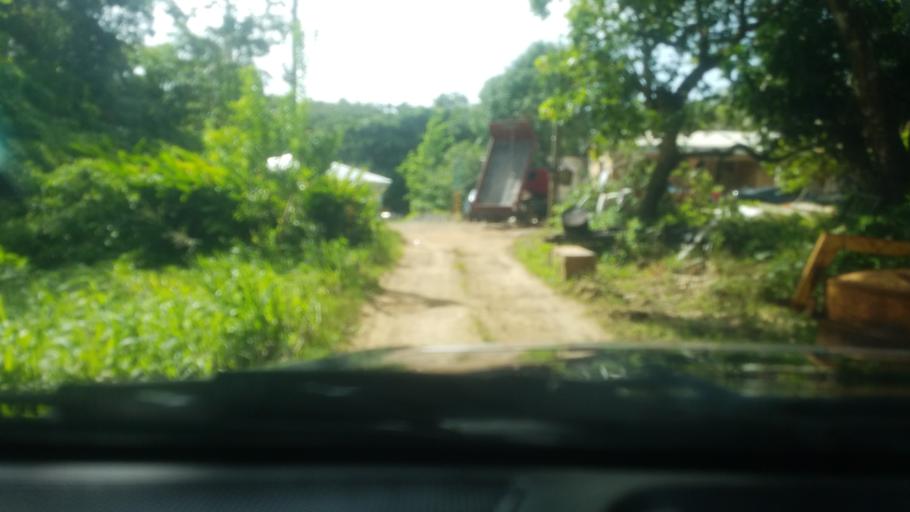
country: LC
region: Micoud Quarter
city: Micoud
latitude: 13.7963
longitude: -60.9250
